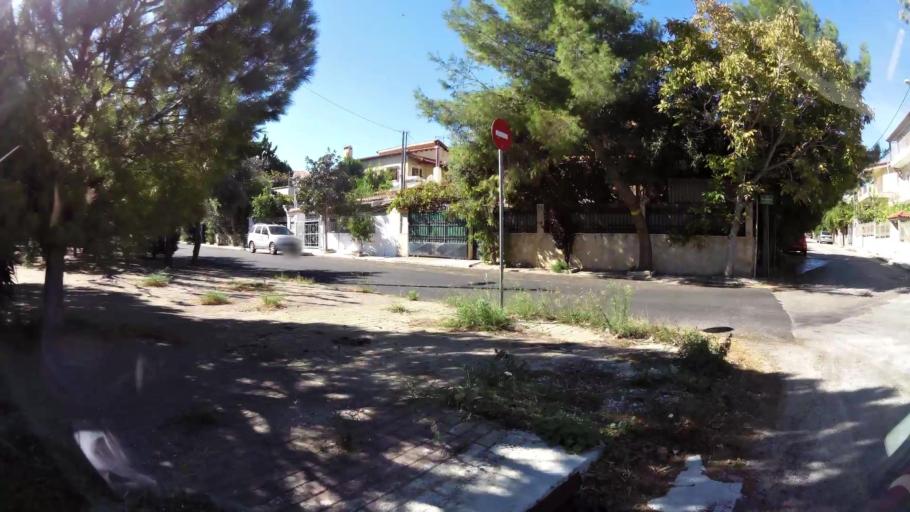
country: GR
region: Attica
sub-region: Nomarchia Anatolikis Attikis
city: Leondarion
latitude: 37.9912
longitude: 23.8635
